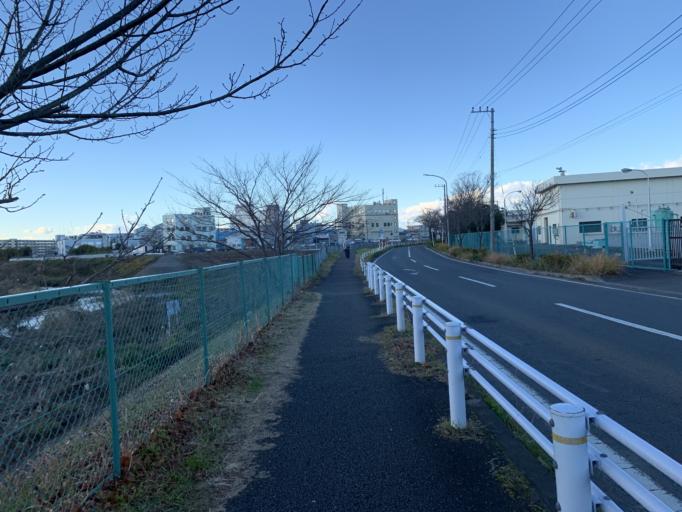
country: JP
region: Tokyo
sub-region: Machida-shi
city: Machida
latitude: 35.5140
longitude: 139.5521
